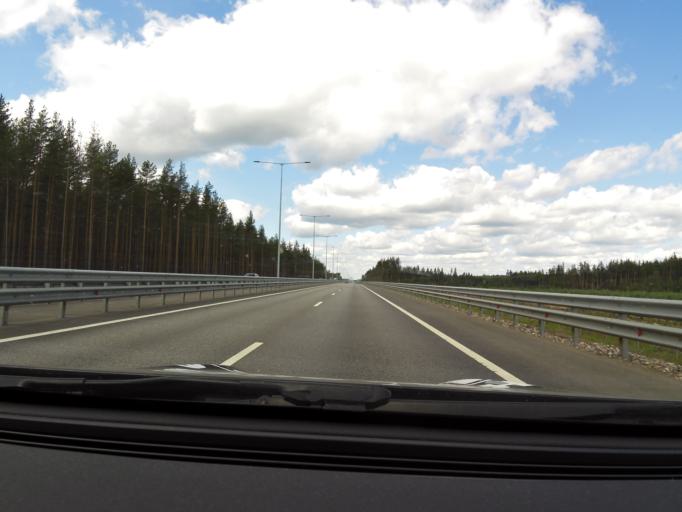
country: RU
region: Tverskaya
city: Vyshniy Volochek
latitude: 57.4263
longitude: 34.4842
